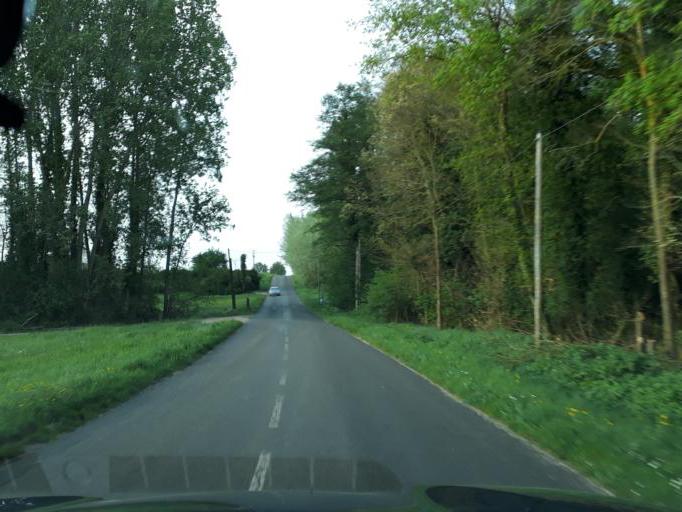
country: FR
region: Centre
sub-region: Departement du Loir-et-Cher
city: Saint-Laurent-Nouan
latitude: 47.7283
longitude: 1.6355
